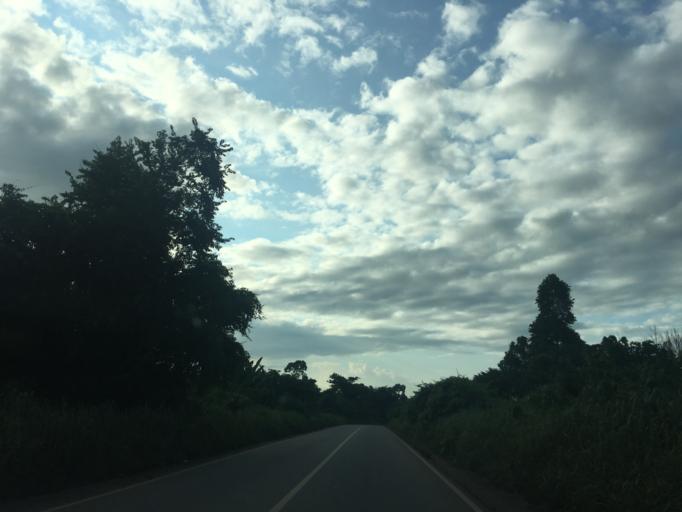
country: GH
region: Western
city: Bibiani
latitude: 6.3473
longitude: -2.2769
